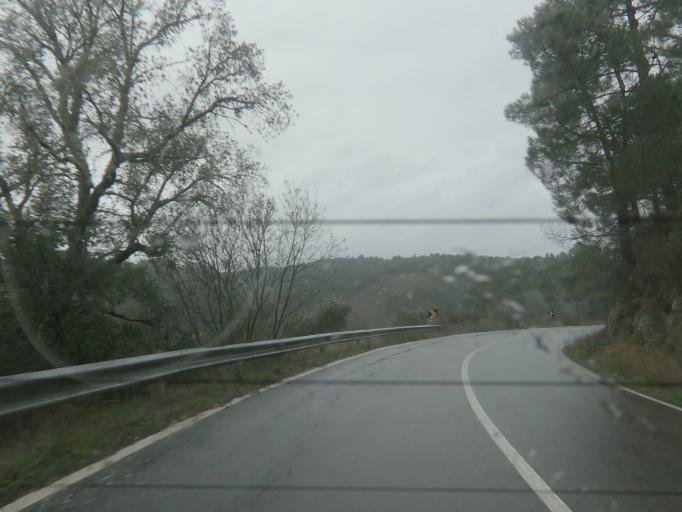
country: PT
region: Vila Real
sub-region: Vila Real
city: Vila Real
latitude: 41.2473
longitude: -7.6866
